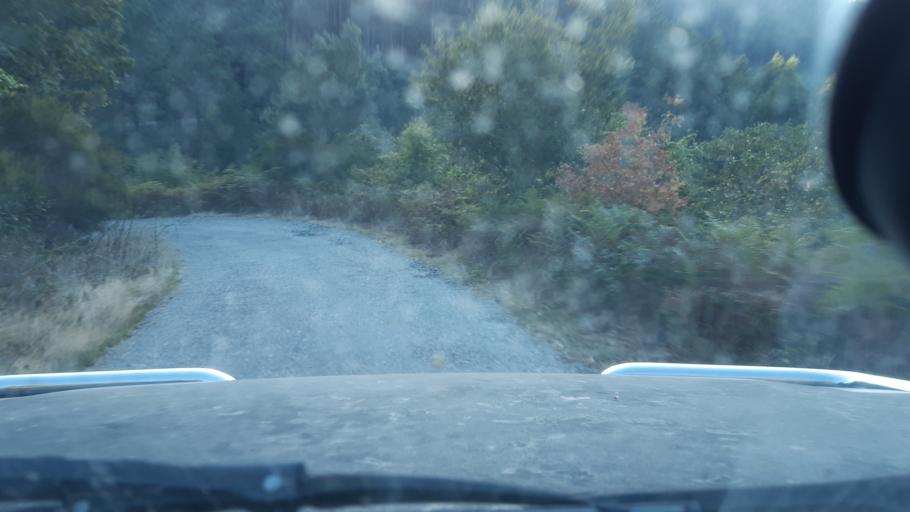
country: PT
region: Viseu
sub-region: Mortagua
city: Mortagua
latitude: 40.5208
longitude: -8.2475
